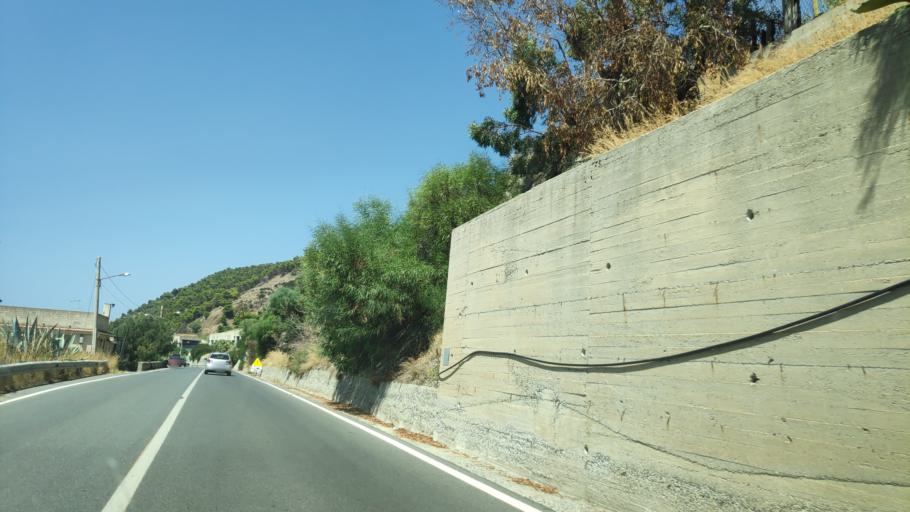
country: IT
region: Calabria
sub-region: Provincia di Reggio Calabria
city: Palizzi Marina
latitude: 37.9201
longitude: 15.9755
